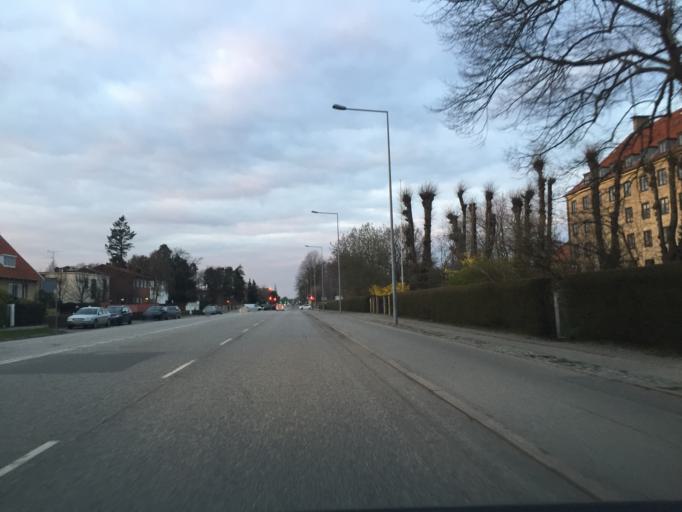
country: DK
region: Capital Region
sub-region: Gentofte Kommune
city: Charlottenlund
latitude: 55.7263
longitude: 12.5550
